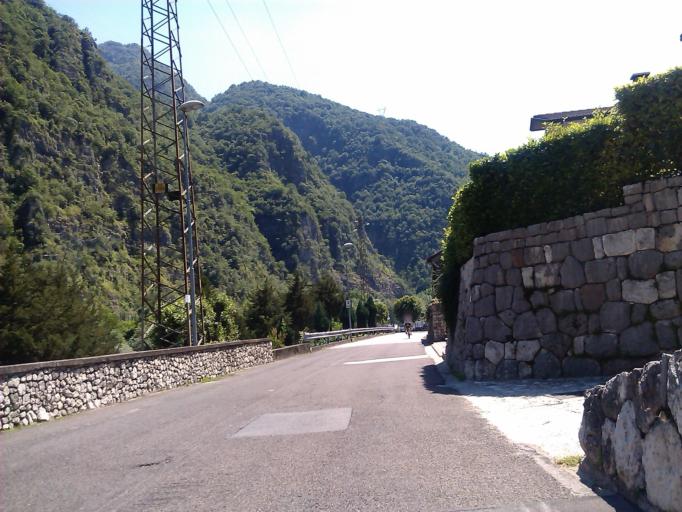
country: IT
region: Veneto
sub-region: Provincia di Vicenza
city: Valstagna
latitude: 45.8766
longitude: 11.6766
